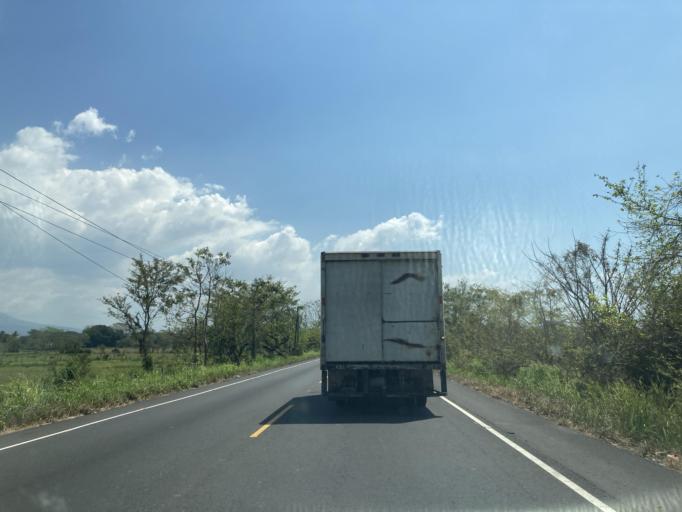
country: GT
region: Santa Rosa
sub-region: Municipio de Taxisco
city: Taxisco
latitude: 14.0947
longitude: -90.5890
